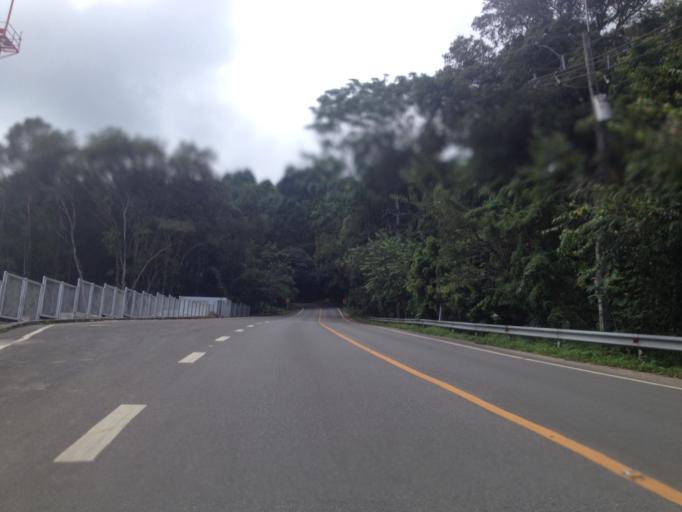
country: TH
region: Chiang Mai
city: Chiang Mai
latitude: 18.8022
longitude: 98.9042
